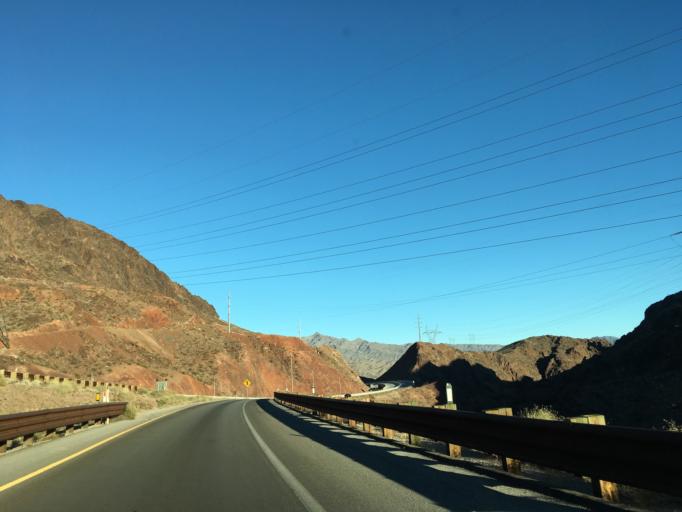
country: US
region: Nevada
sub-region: Clark County
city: Boulder City
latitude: 36.0111
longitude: -114.7725
